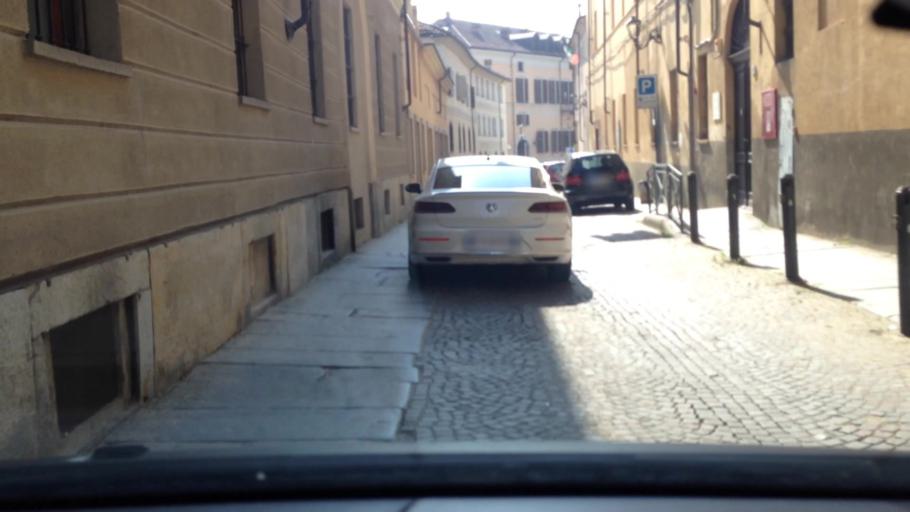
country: IT
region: Piedmont
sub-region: Provincia di Asti
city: Asti
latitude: 44.8973
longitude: 8.2004
